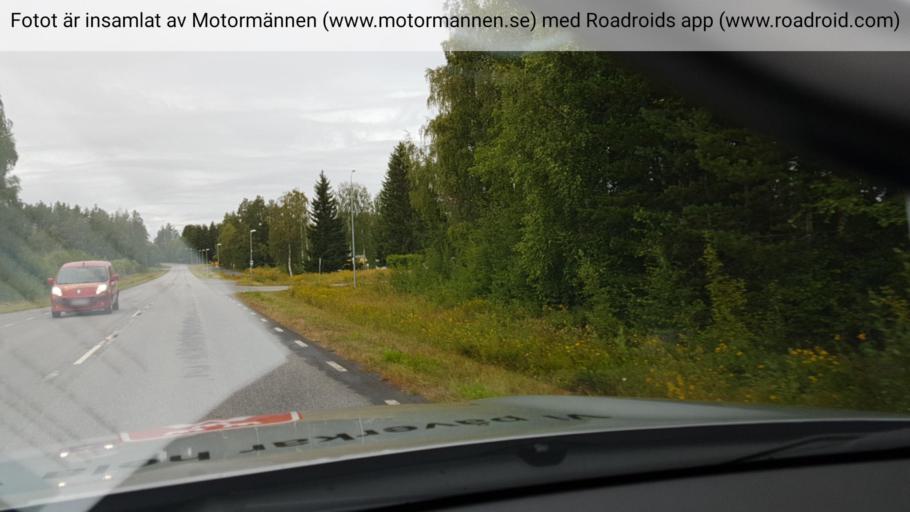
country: SE
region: Norrbotten
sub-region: Bodens Kommun
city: Boden
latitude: 65.8145
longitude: 21.6229
